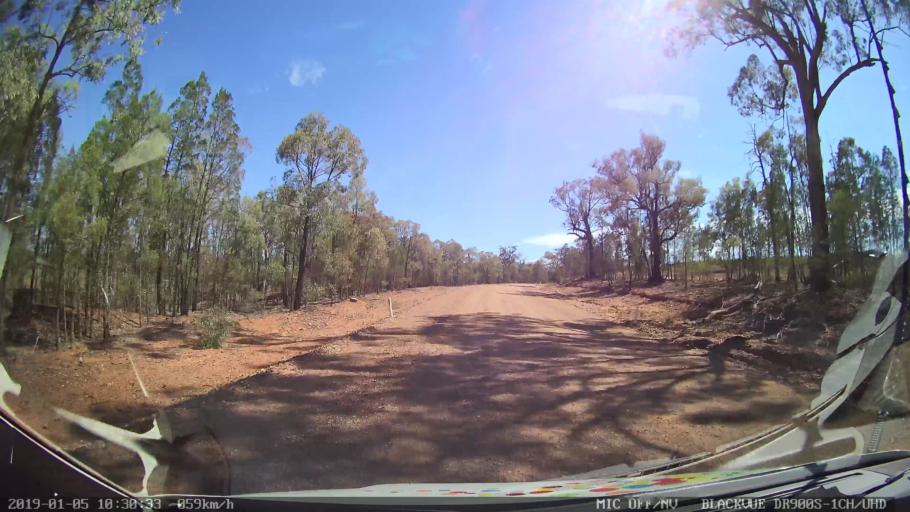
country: AU
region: New South Wales
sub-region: Gilgandra
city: Gilgandra
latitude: -31.5313
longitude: 148.9248
